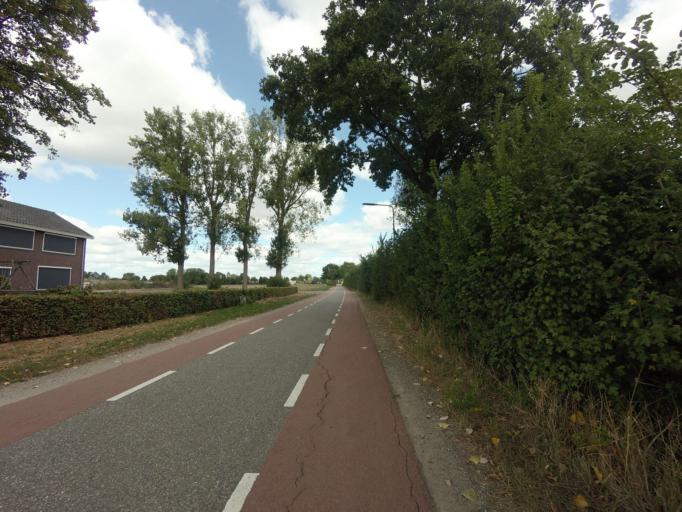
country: NL
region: North Brabant
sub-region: Gemeente Landerd
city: Schaijk
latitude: 51.7989
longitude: 5.6183
